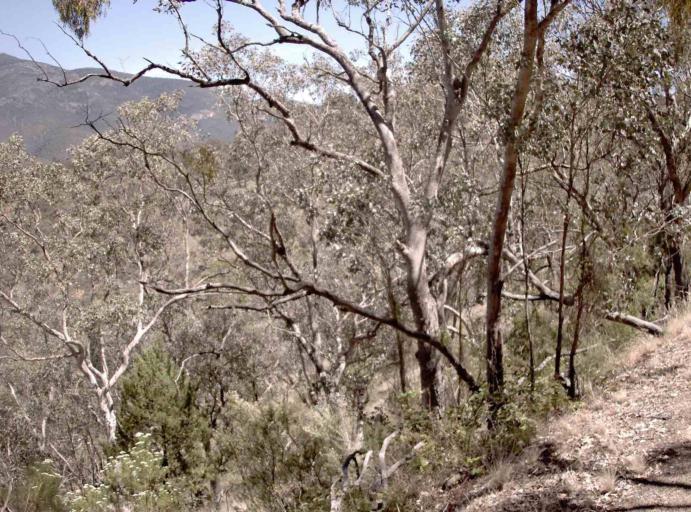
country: AU
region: New South Wales
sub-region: Snowy River
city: Jindabyne
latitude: -36.9459
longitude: 148.3385
